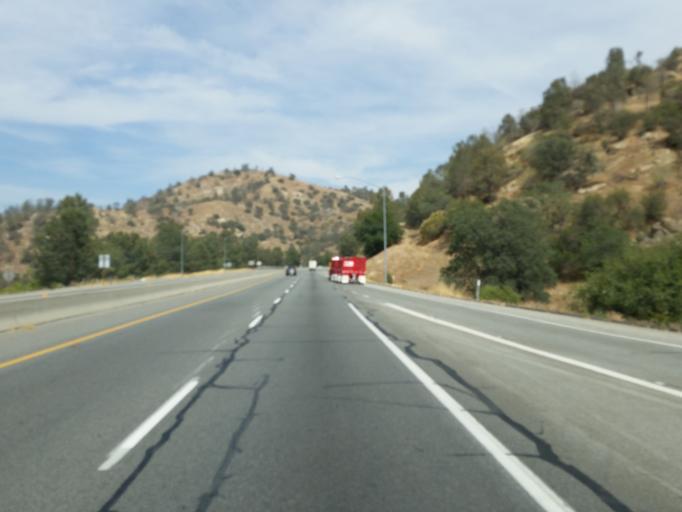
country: US
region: California
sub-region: Kern County
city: Bear Valley Springs
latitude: 35.2229
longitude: -118.5648
